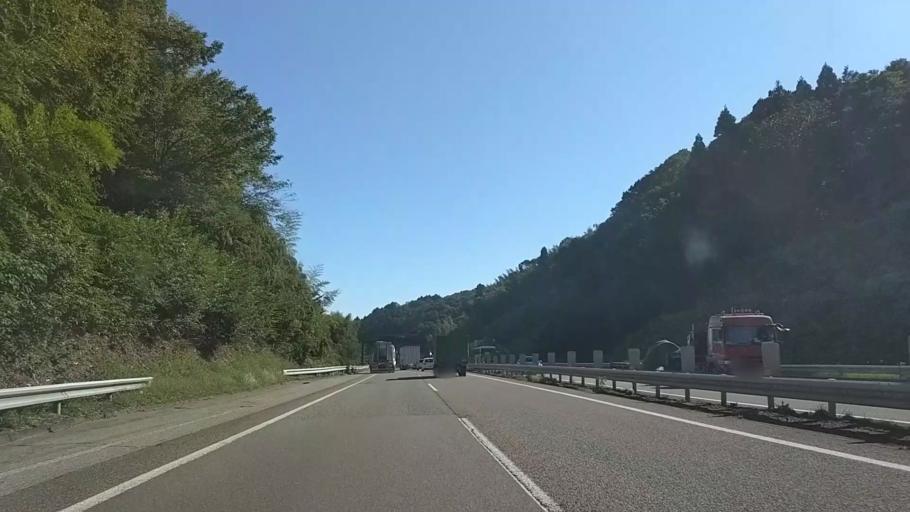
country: JP
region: Toyama
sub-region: Oyabe Shi
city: Oyabe
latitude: 36.6146
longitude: 136.8172
